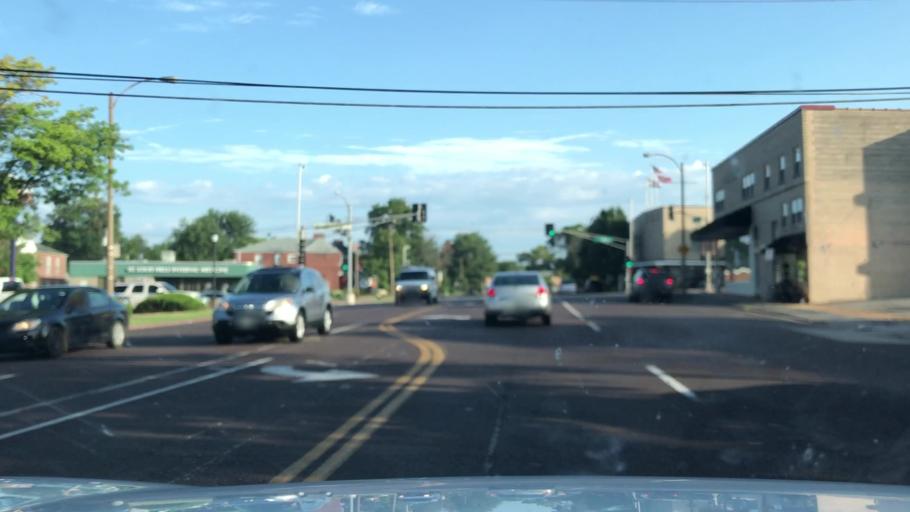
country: US
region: Missouri
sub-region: Saint Louis County
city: Shrewsbury
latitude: 38.5885
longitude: -90.3089
